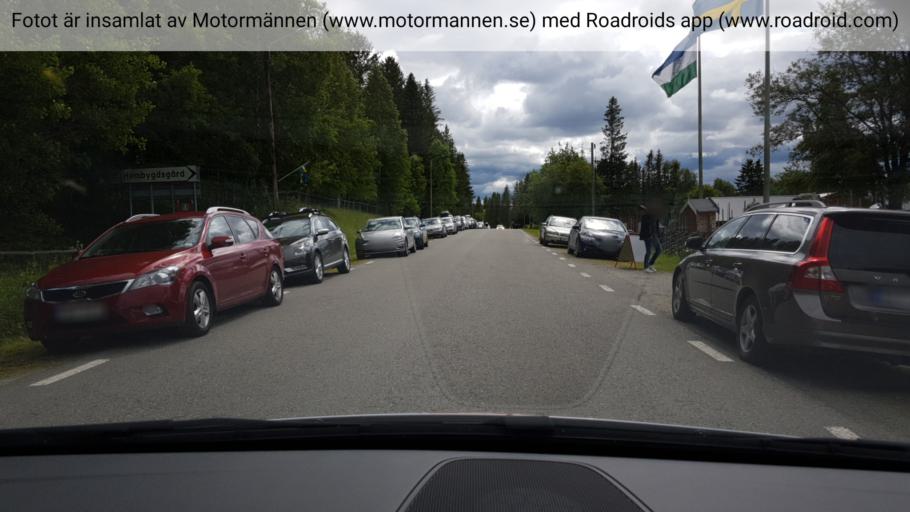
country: SE
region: Jaemtland
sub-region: Bergs Kommun
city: Hoverberg
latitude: 62.5244
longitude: 14.1871
